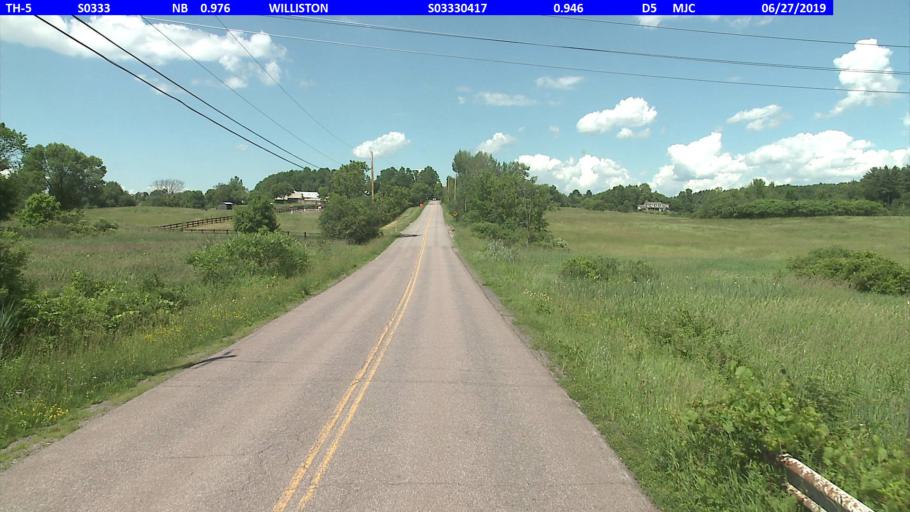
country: US
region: Vermont
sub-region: Chittenden County
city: South Burlington
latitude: 44.4149
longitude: -73.1377
